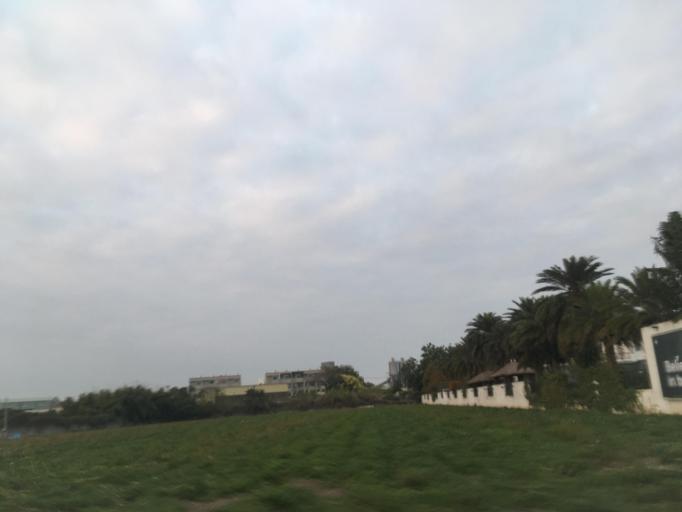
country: TW
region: Taiwan
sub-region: Yunlin
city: Douliu
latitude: 23.7034
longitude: 120.4490
